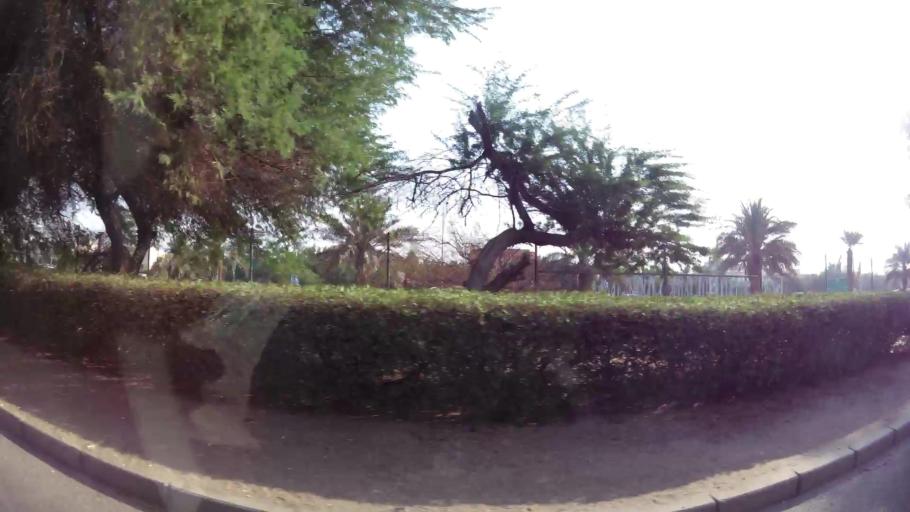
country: KW
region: Muhafazat Hawalli
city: Salwa
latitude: 29.2797
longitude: 48.0777
